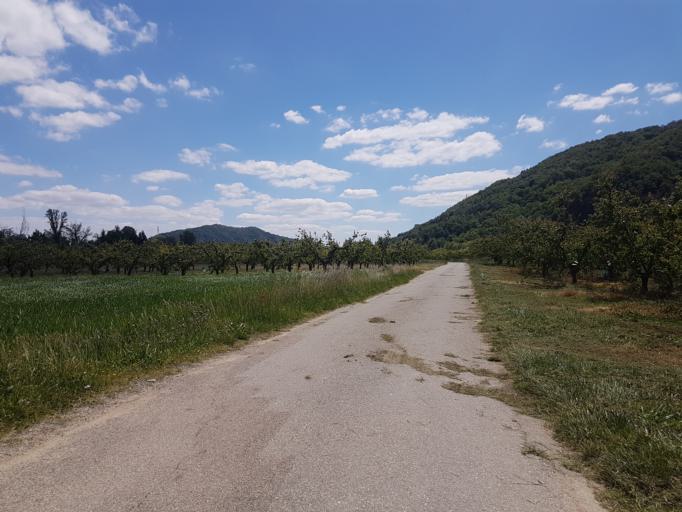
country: FR
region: Rhone-Alpes
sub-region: Departement de l'Ardeche
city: Saint-Jean-de-Muzols
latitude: 45.1117
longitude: 4.8120
